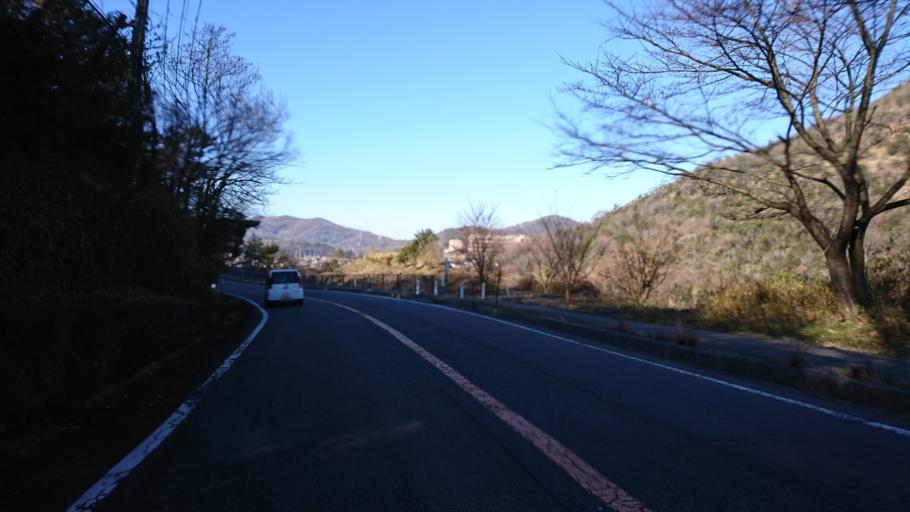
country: JP
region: Hyogo
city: Kakogawacho-honmachi
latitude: 34.8395
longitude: 134.8463
